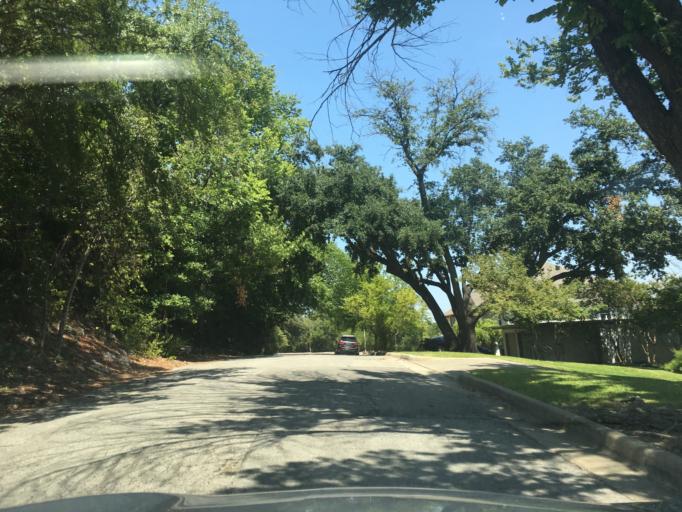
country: US
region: Texas
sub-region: Tarrant County
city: Fort Worth
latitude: 32.7119
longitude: -97.3541
